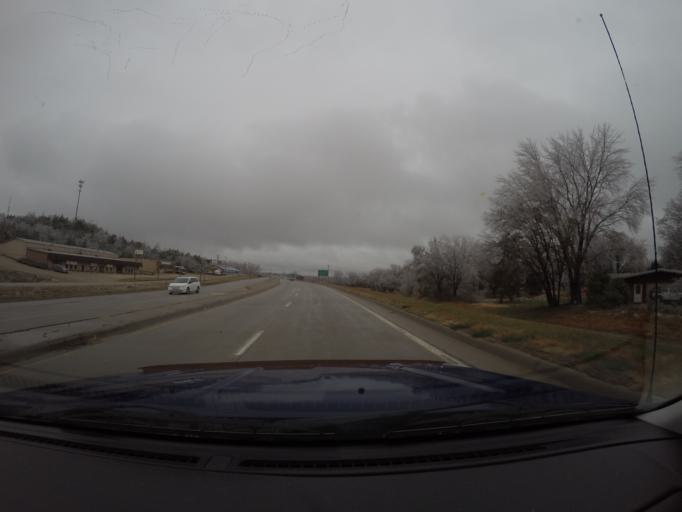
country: US
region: Kansas
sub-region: Riley County
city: Manhattan
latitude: 39.1734
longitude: -96.5484
